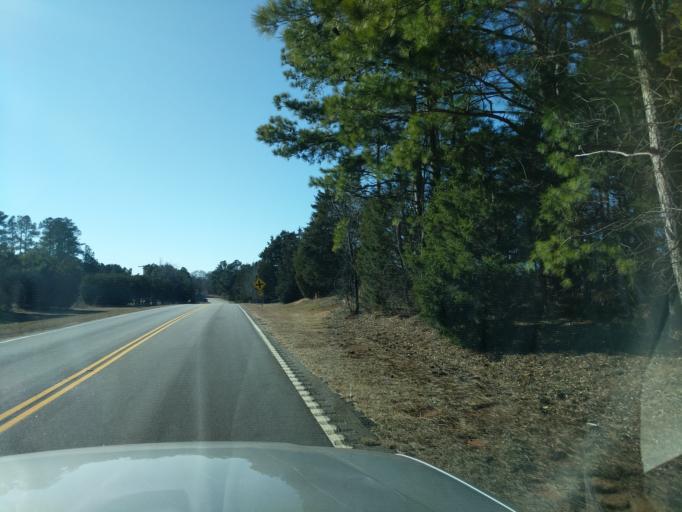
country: US
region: South Carolina
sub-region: Anderson County
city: Homeland Park
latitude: 34.4412
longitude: -82.7293
